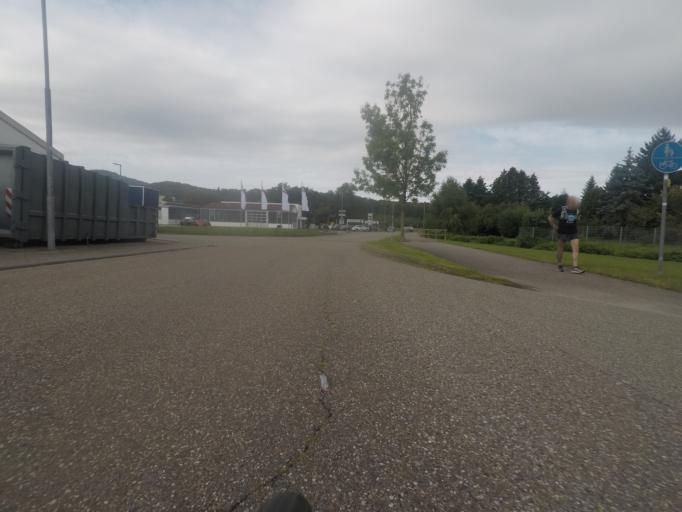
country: DE
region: Baden-Wuerttemberg
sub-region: Karlsruhe Region
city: Gernsbach
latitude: 48.7758
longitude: 8.3449
